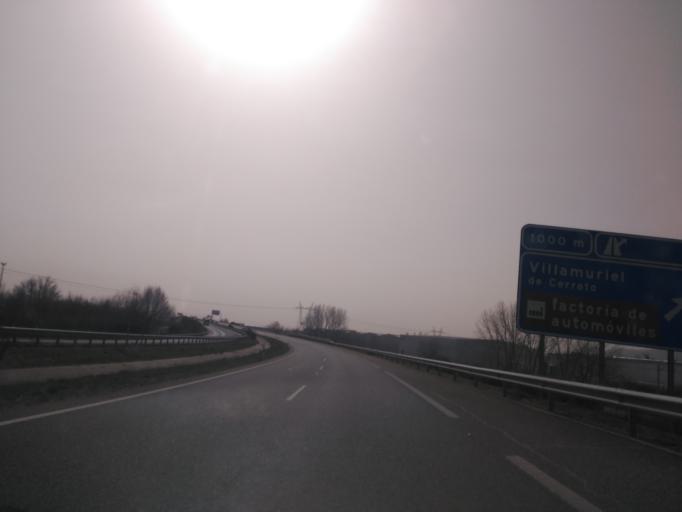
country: ES
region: Castille and Leon
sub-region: Provincia de Palencia
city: Villamuriel de Cerrato
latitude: 41.9672
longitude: -4.5047
